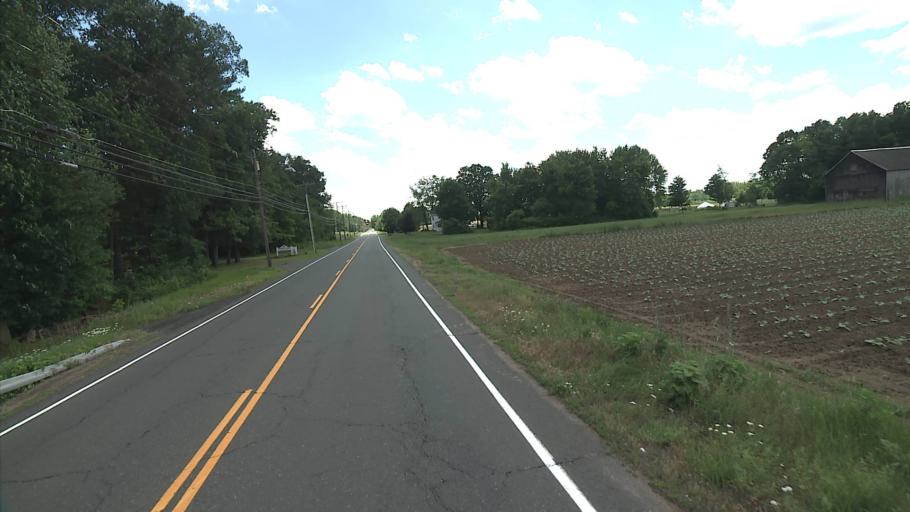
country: US
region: Connecticut
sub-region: Hartford County
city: Hazardville
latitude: 42.0031
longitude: -72.5418
